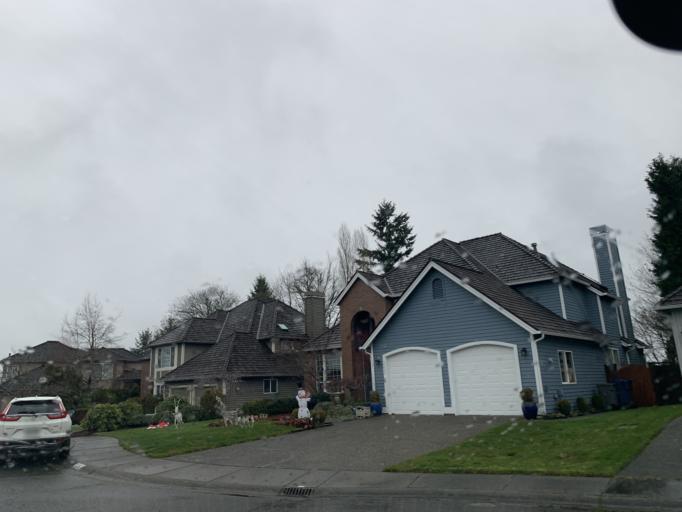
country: US
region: Washington
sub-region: King County
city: Kingsgate
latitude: 47.7333
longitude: -122.1617
